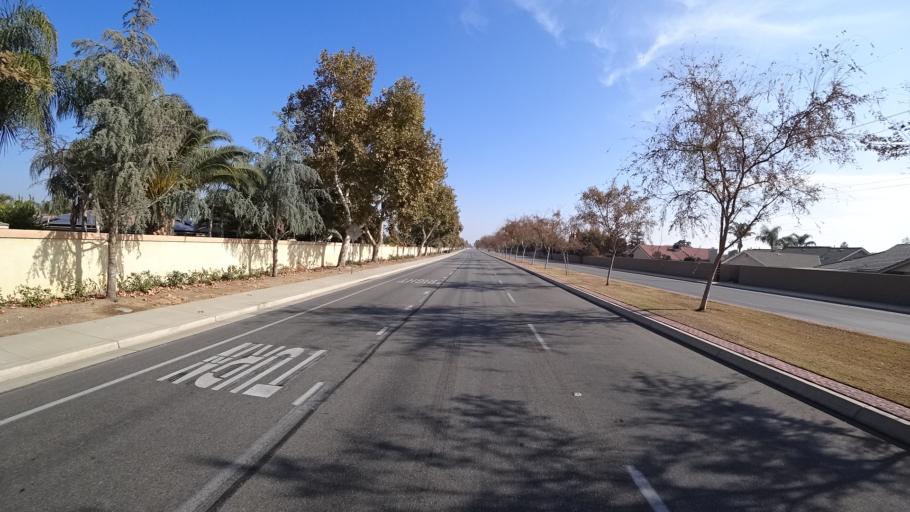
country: US
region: California
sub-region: Kern County
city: Rosedale
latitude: 35.3545
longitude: -119.1616
